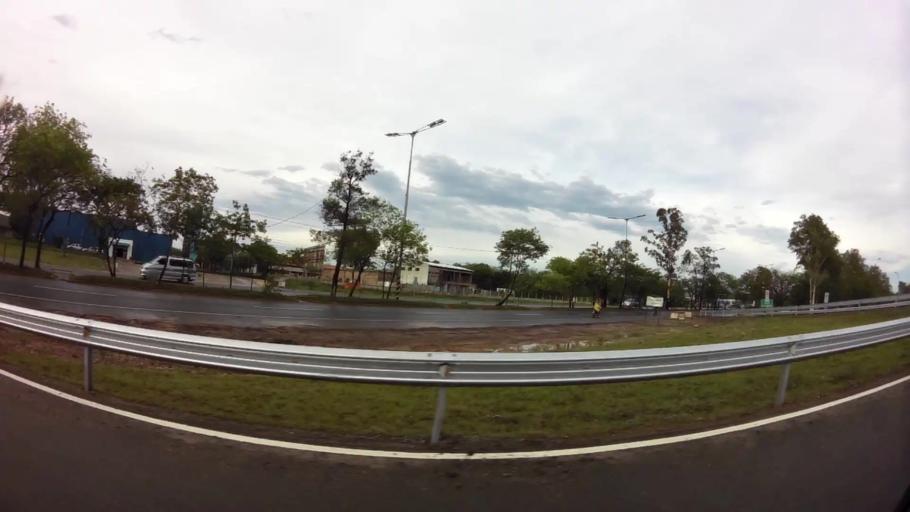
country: PY
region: Central
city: Fernando de la Mora
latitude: -25.2627
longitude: -57.5206
